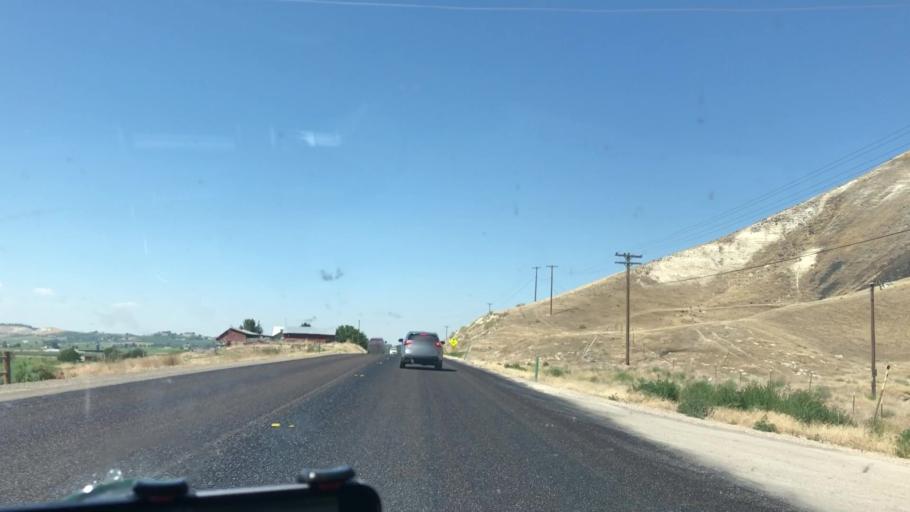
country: US
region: Idaho
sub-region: Owyhee County
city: Marsing
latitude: 43.5560
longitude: -116.7922
